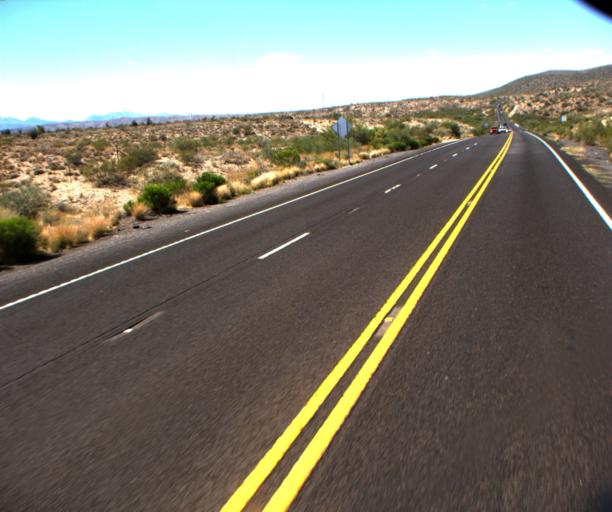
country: US
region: Arizona
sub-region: Mohave County
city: Kingman
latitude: 34.9143
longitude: -113.6569
